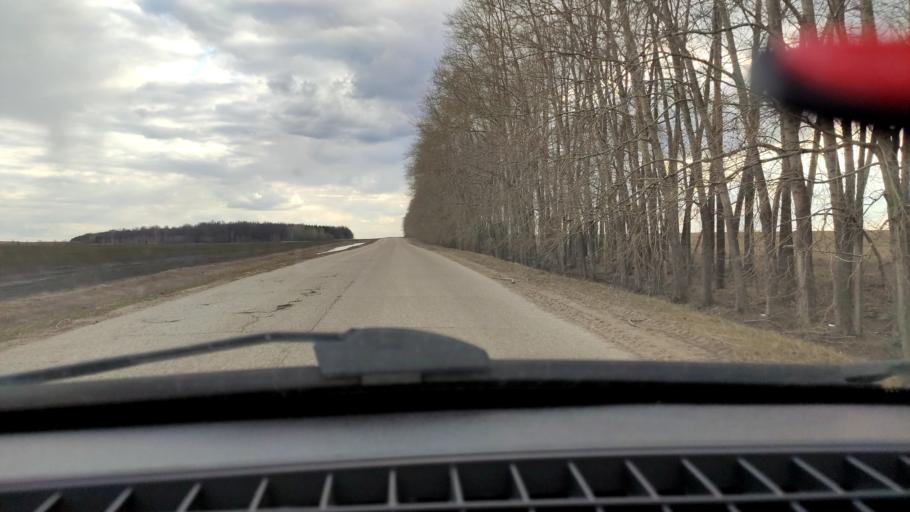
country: RU
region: Bashkortostan
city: Karmaskaly
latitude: 54.3061
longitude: 55.9366
